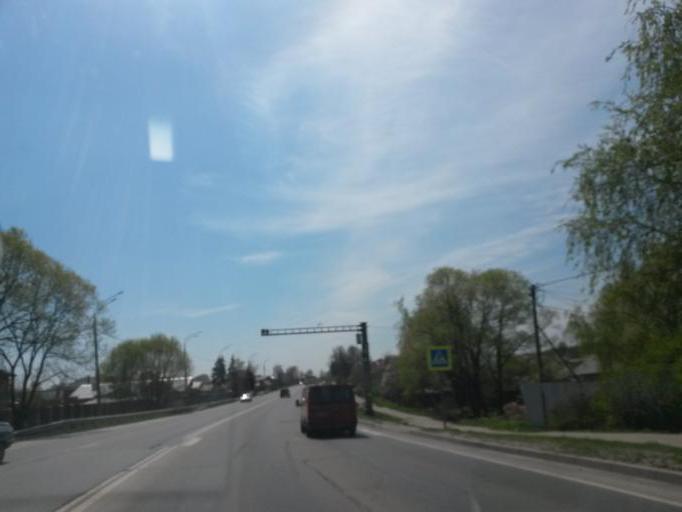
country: RU
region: Moskovskaya
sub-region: Podol'skiy Rayon
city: Podol'sk
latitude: 55.3998
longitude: 37.5509
